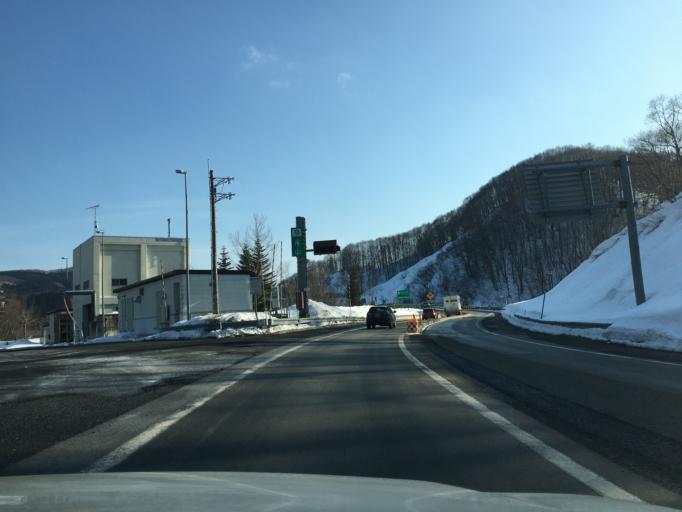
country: JP
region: Yamagata
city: Sagae
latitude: 38.4541
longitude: 139.9928
